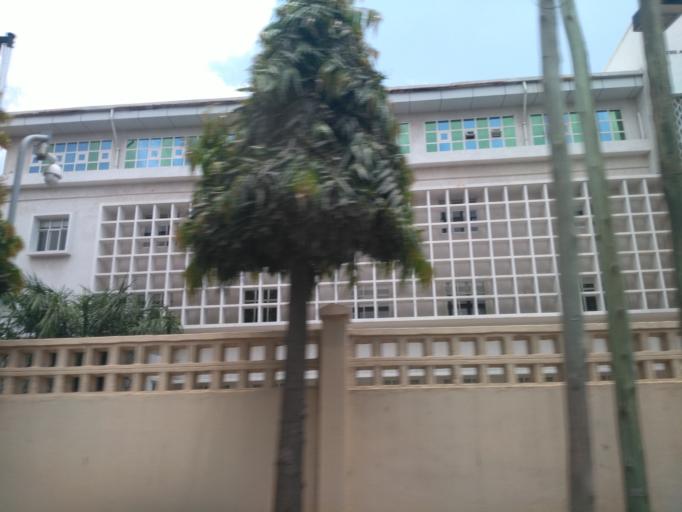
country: TZ
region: Dar es Salaam
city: Dar es Salaam
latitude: -6.8000
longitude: 39.2799
